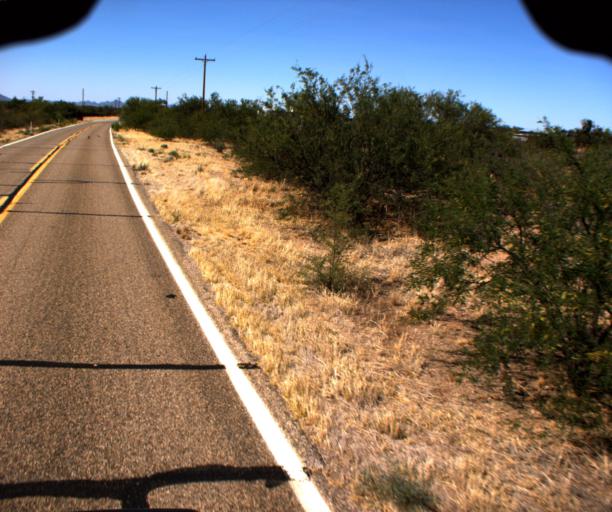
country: US
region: Arizona
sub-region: Pima County
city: Three Points
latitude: 31.8806
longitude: -111.3961
